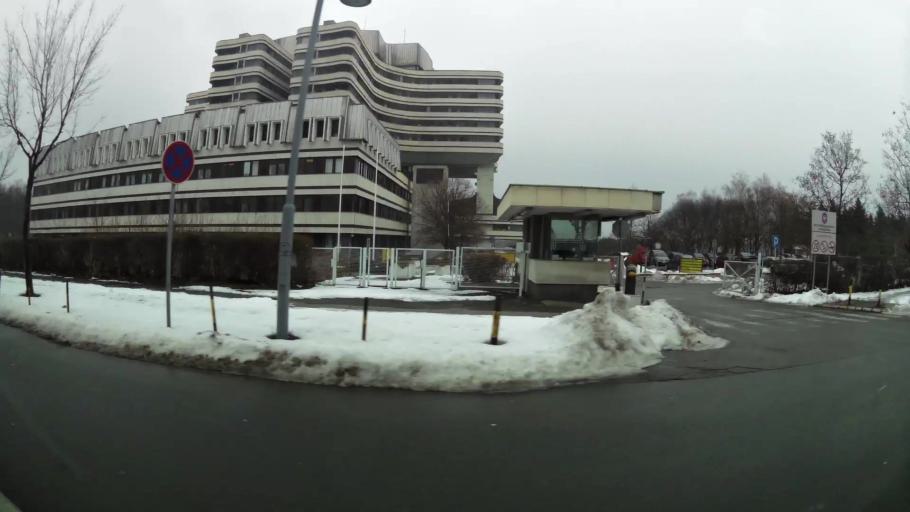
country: RS
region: Central Serbia
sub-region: Belgrade
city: Vozdovac
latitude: 44.7631
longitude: 20.4659
